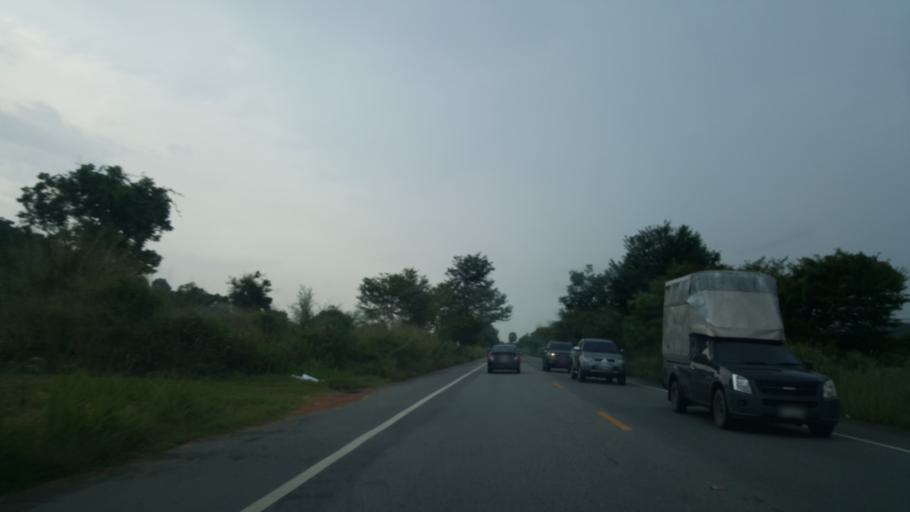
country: TH
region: Chon Buri
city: Sattahip
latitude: 12.7312
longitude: 100.9544
